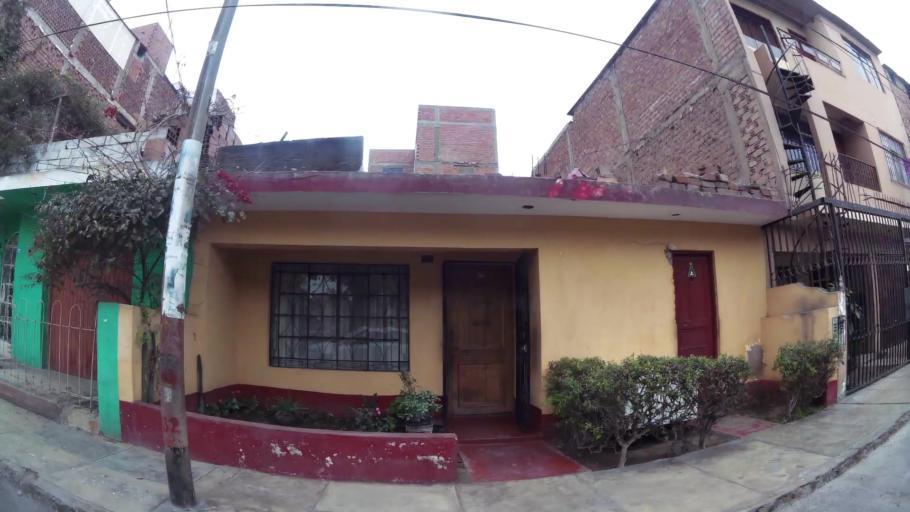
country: PE
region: Lima
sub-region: Lima
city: Surco
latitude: -12.1085
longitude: -77.0119
